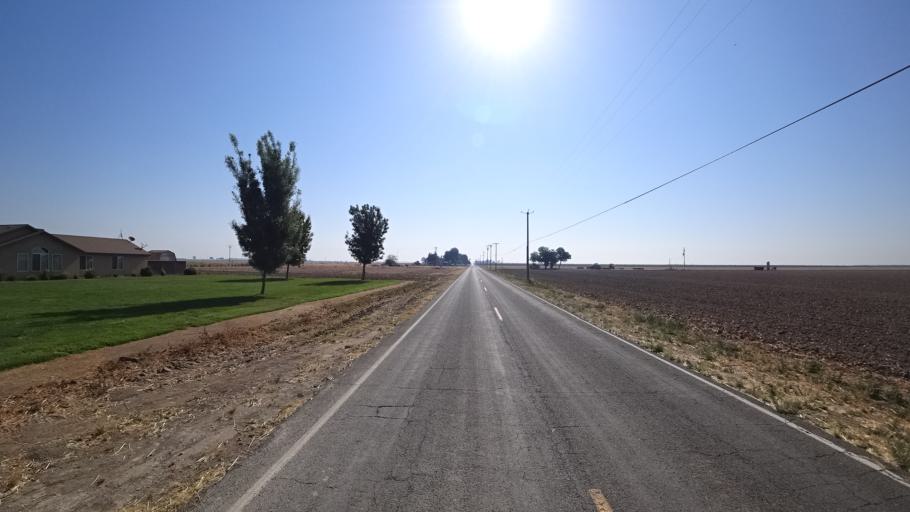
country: US
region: California
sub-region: Kings County
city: Lucerne
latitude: 36.4014
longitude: -119.5577
